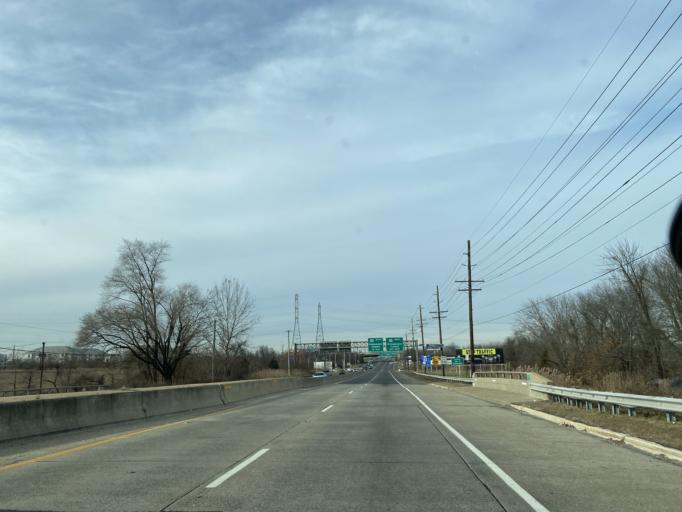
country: US
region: New Jersey
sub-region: Burlington County
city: Cinnaminson
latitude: 39.9776
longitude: -75.0124
